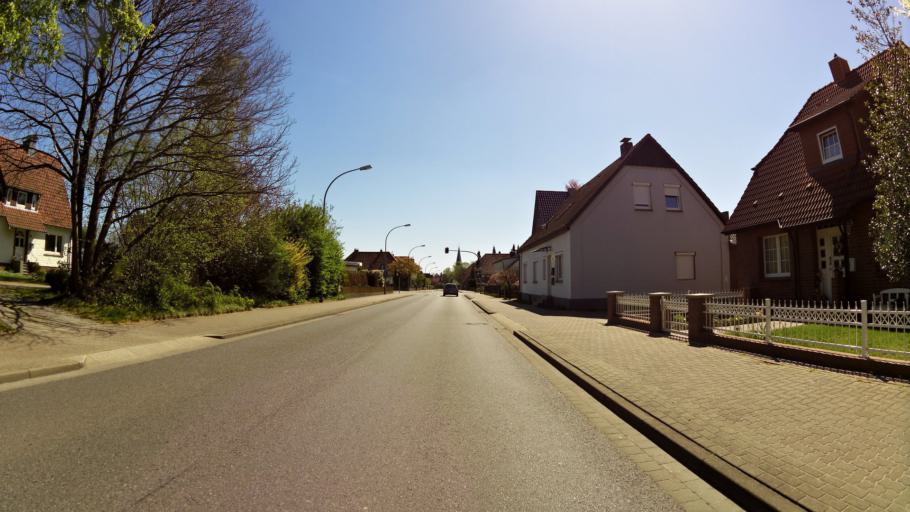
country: DE
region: Lower Saxony
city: Soltau
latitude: 52.9916
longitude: 9.8281
